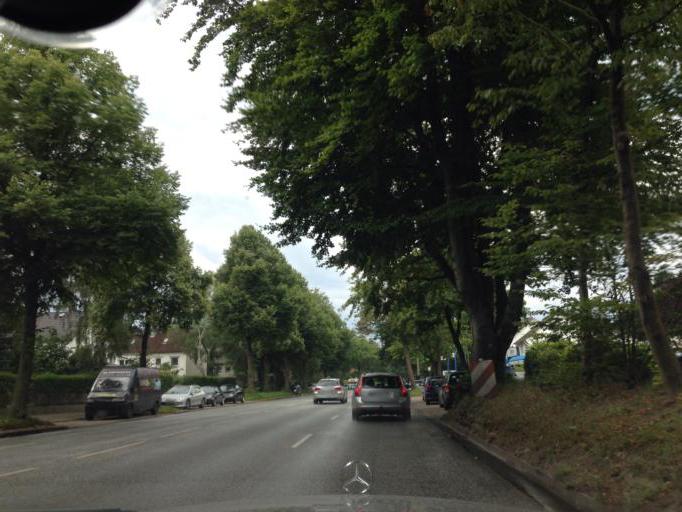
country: DE
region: Hamburg
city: Sasel
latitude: 53.6465
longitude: 10.1016
